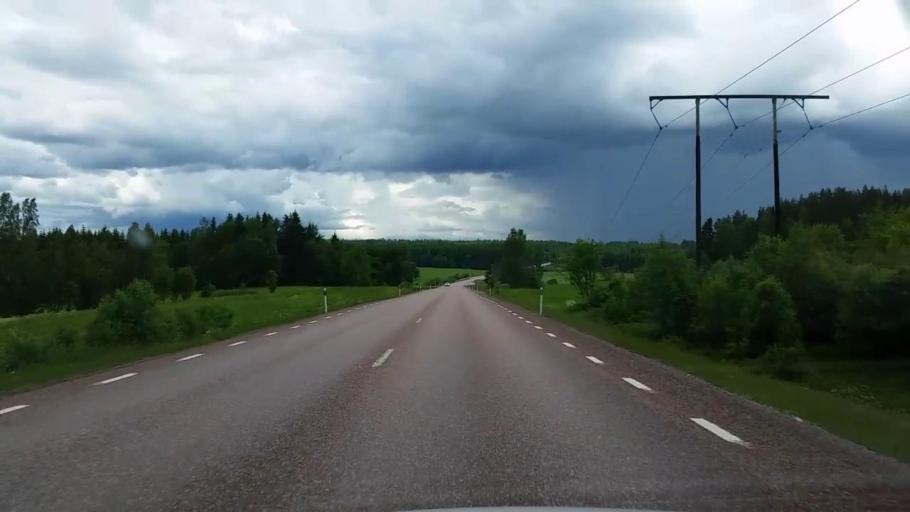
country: SE
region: Gaevleborg
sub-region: Hofors Kommun
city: Hofors
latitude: 60.5343
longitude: 16.4587
